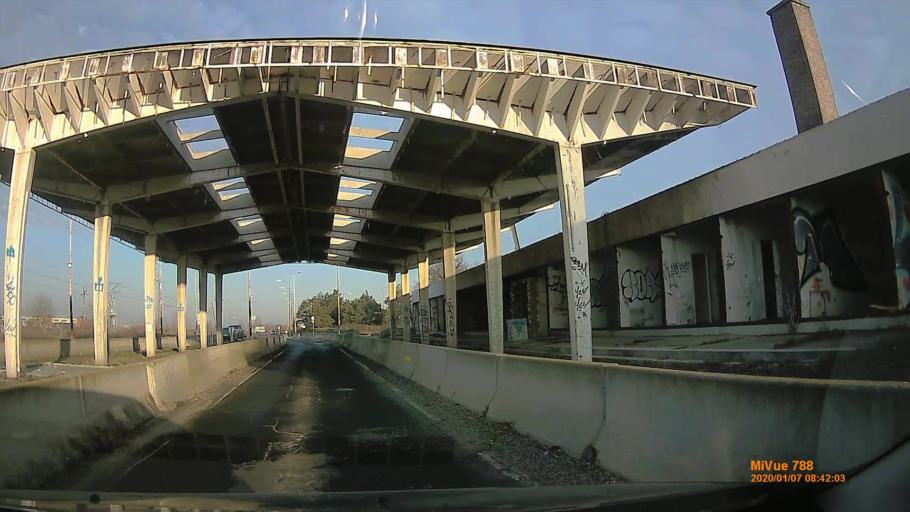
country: HU
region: Gyor-Moson-Sopron
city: Rajka
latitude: 48.0130
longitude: 17.1803
